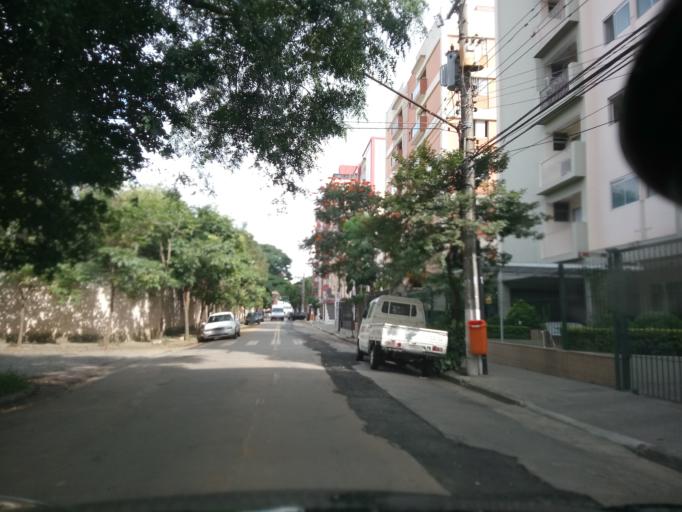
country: BR
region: Sao Paulo
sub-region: Santo Andre
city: Santo Andre
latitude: -23.6510
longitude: -46.5682
